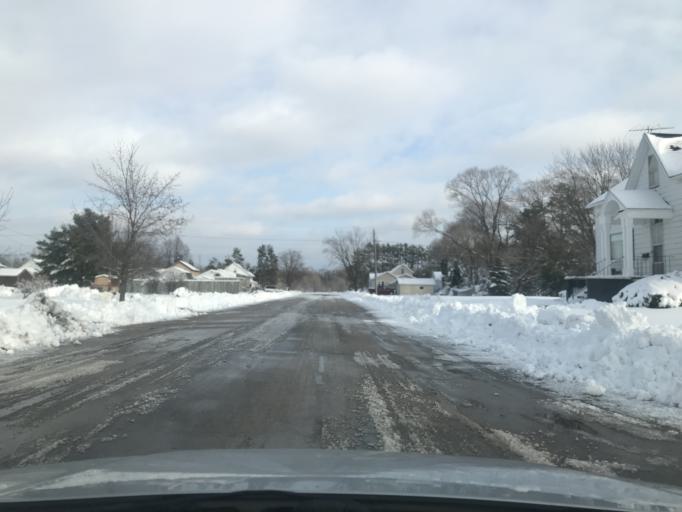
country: US
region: Wisconsin
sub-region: Marinette County
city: Peshtigo
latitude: 45.0486
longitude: -87.7507
